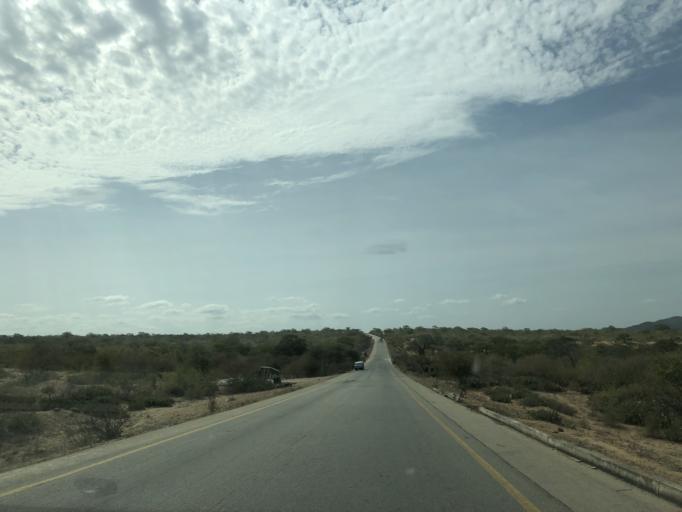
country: AO
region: Benguela
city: Benguela
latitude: -13.0163
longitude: 13.7204
